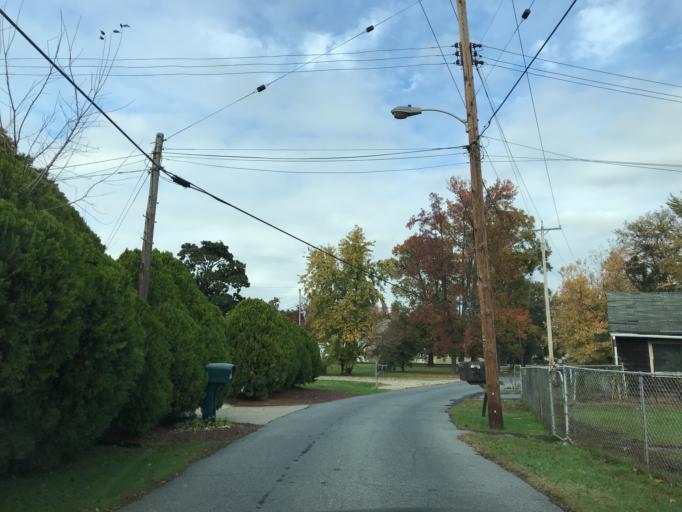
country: US
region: Maryland
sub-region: Baltimore County
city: Bowleys Quarters
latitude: 39.3055
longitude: -76.3944
